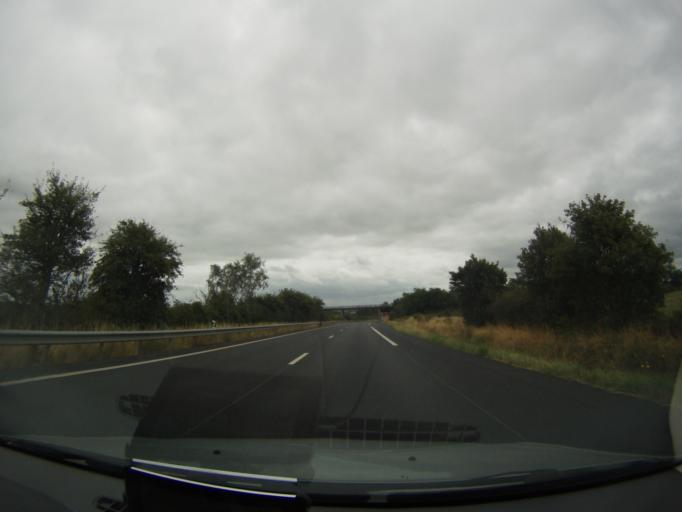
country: FR
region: Brittany
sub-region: Departement d'Ille-et-Vilaine
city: Grand-Fougeray
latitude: 47.7083
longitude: -1.7055
